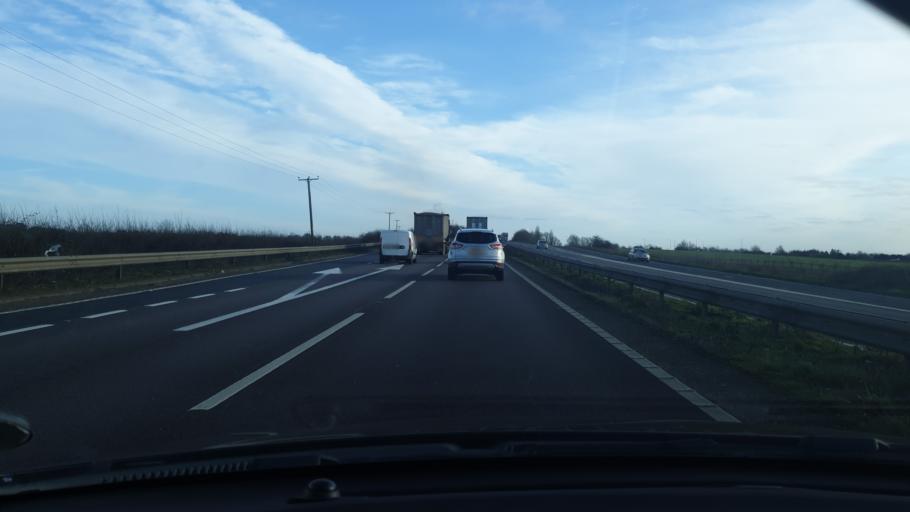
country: GB
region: England
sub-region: Suffolk
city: Bury St Edmunds
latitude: 52.2576
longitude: 0.6665
